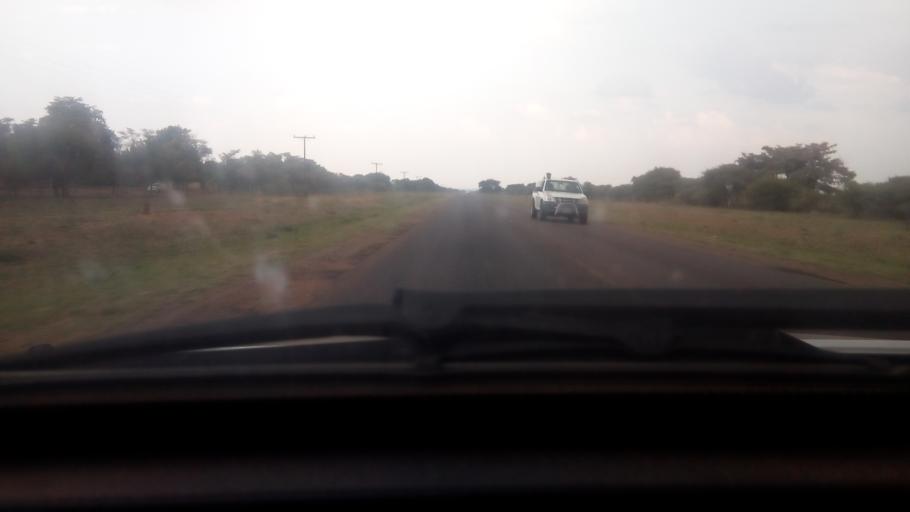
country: BW
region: Kweneng
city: Metsemotlhaba
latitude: -24.4856
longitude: 25.7367
